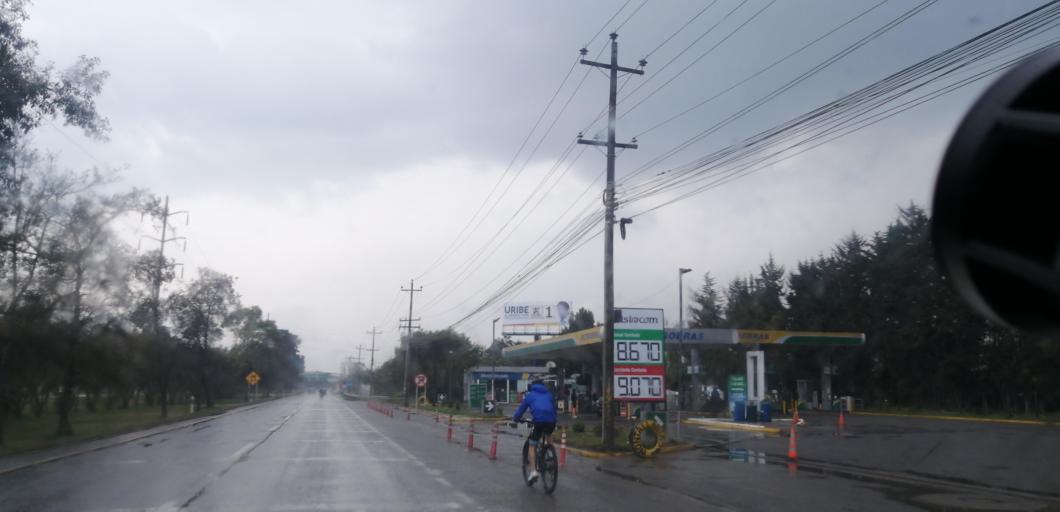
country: CO
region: Cundinamarca
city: Funza
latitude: 4.6972
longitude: -74.2128
